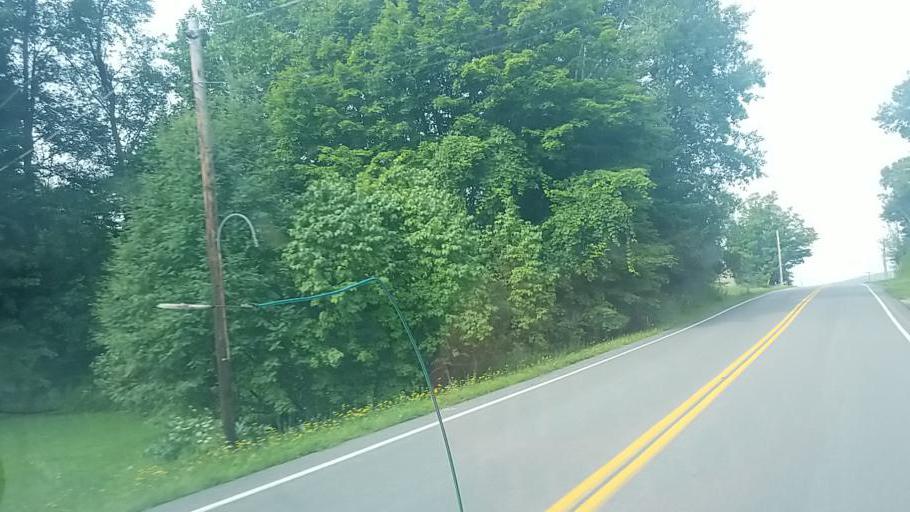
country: US
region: New York
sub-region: Fulton County
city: Gloversville
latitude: 43.1038
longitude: -74.2808
